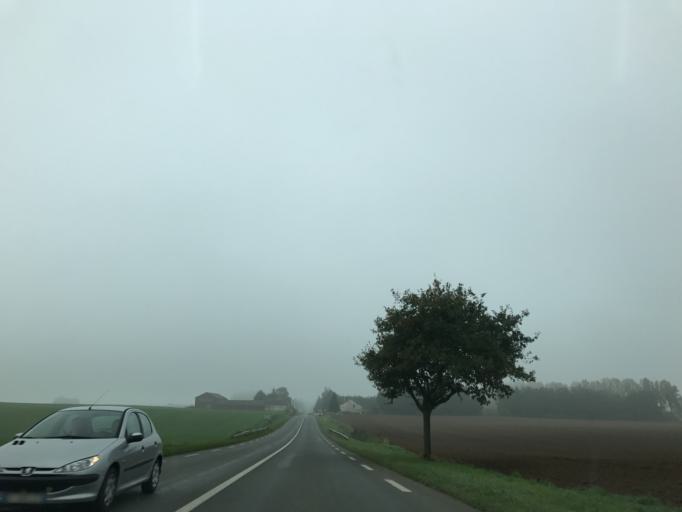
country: FR
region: Nord-Pas-de-Calais
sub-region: Departement du Pas-de-Calais
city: Bapaume
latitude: 50.0702
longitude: 2.8870
